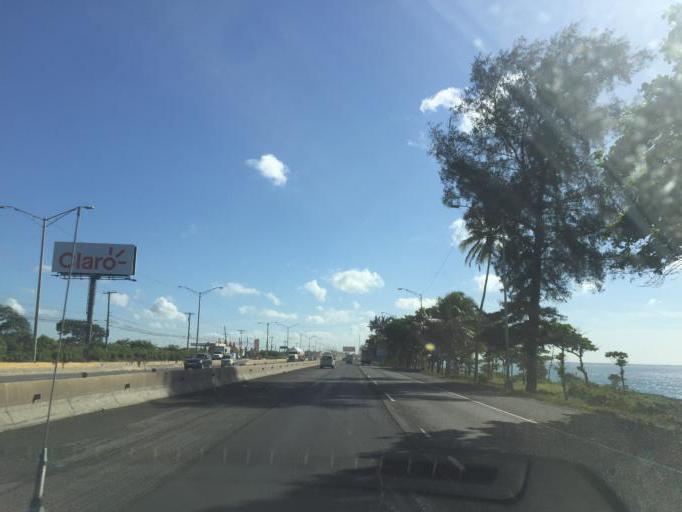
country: DO
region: Santo Domingo
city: Guerra
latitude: 18.4635
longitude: -69.7437
